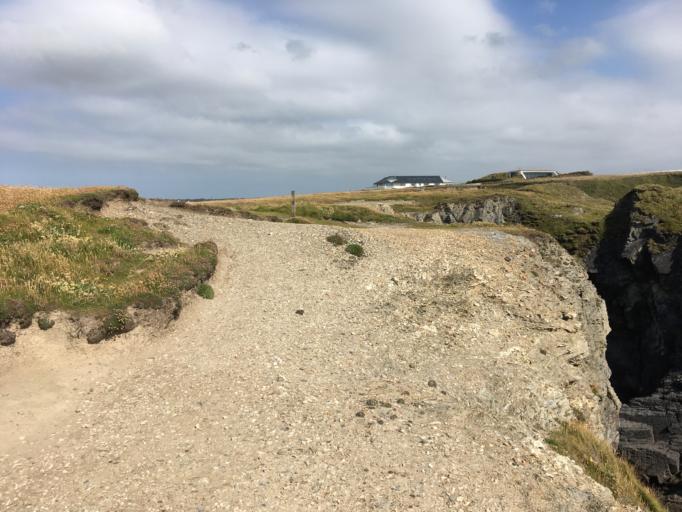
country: GB
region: England
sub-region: Cornwall
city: Padstow
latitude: 50.5245
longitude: -5.0287
